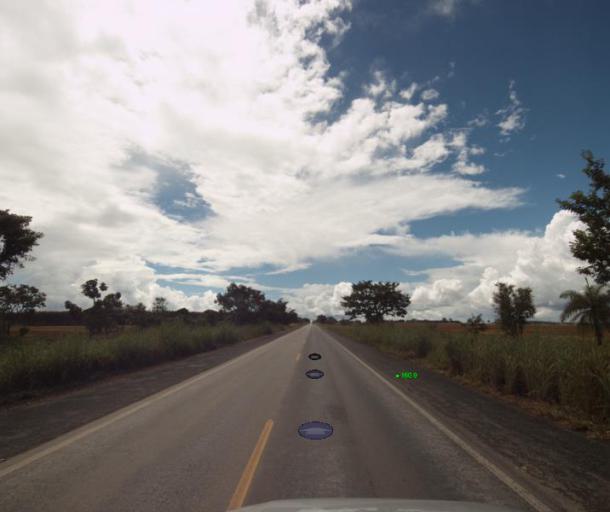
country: BR
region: Goias
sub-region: Uruacu
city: Uruacu
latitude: -14.1807
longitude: -49.1261
